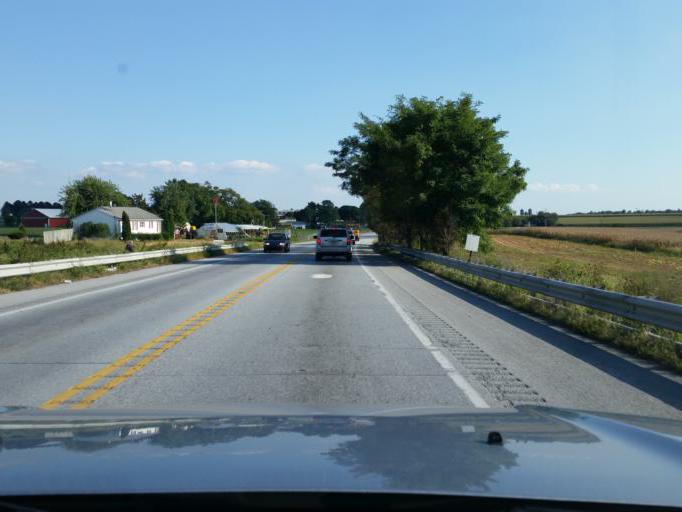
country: US
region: Pennsylvania
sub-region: Chester County
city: Atglen
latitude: 39.9319
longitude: -75.9520
